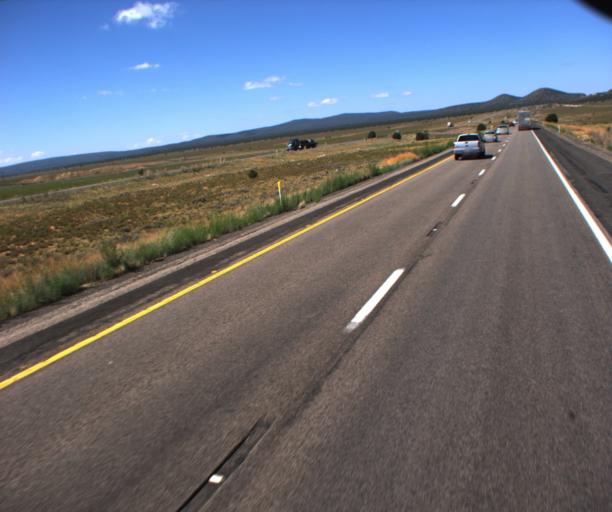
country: US
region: Arizona
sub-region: Mohave County
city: Peach Springs
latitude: 35.3135
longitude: -112.9710
